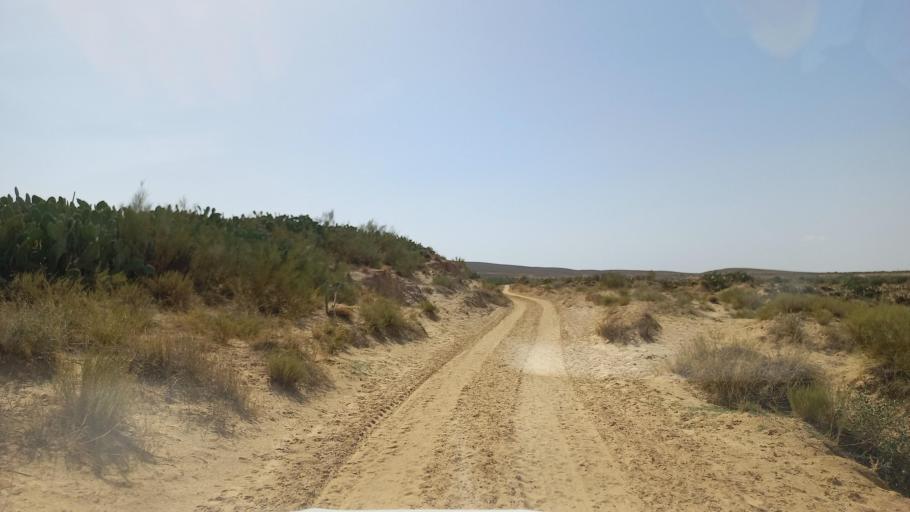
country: TN
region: Al Qasrayn
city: Kasserine
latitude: 35.1995
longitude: 9.0325
